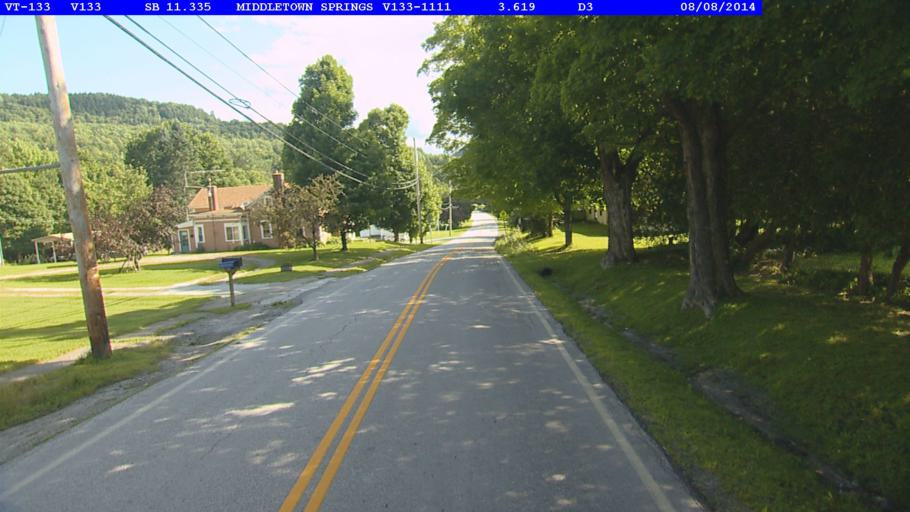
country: US
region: Vermont
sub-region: Rutland County
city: Poultney
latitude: 43.4850
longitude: -73.1184
